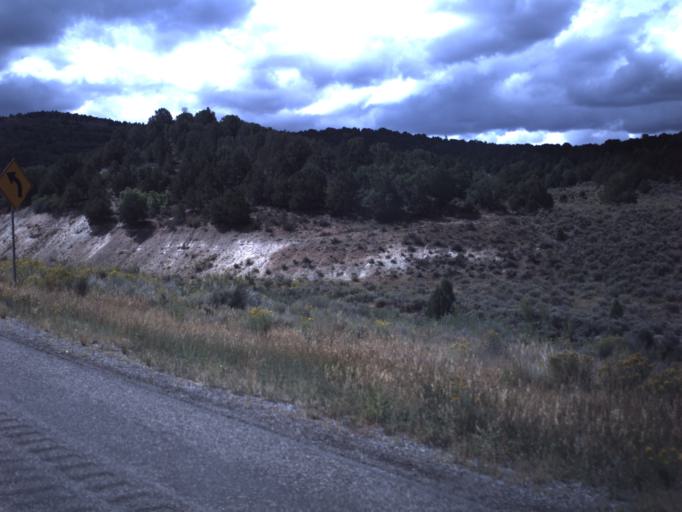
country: US
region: Utah
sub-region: Sevier County
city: Salina
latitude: 38.8269
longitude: -111.5395
